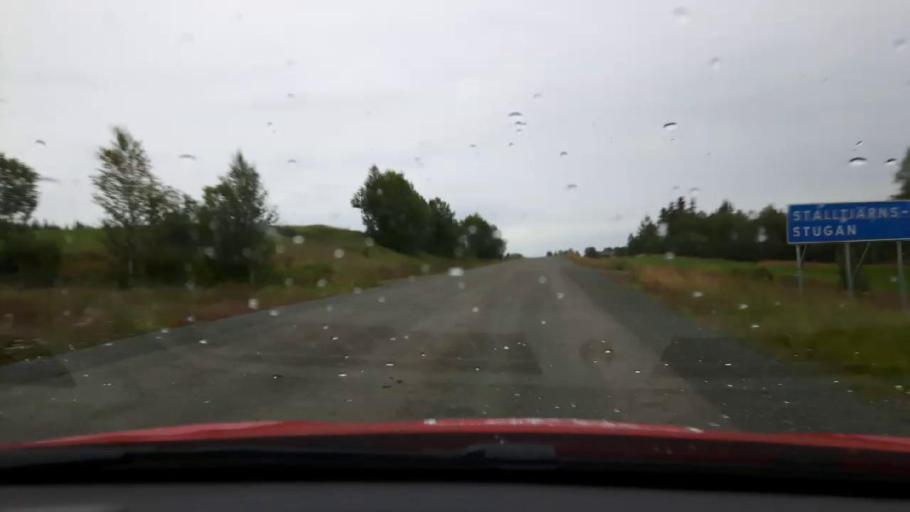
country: SE
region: Jaemtland
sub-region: Are Kommun
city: Are
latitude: 63.4776
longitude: 12.5513
